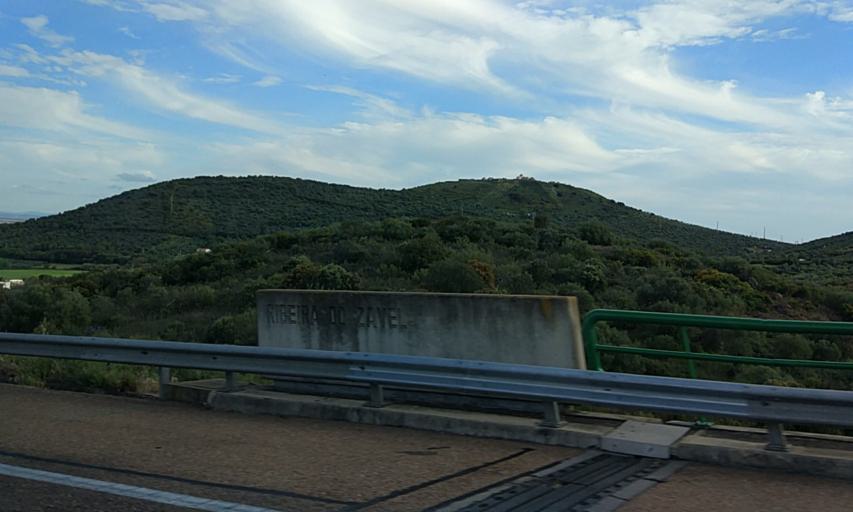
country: PT
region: Portalegre
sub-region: Elvas
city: Elvas
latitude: 38.9083
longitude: -7.1685
